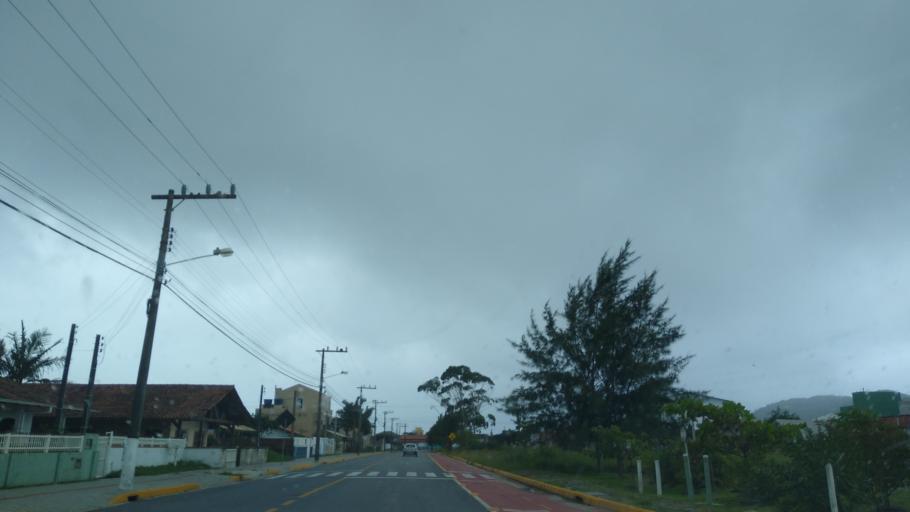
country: BR
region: Santa Catarina
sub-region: Sao Francisco Do Sul
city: Sao Francisco do Sul
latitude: -26.2349
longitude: -48.5112
